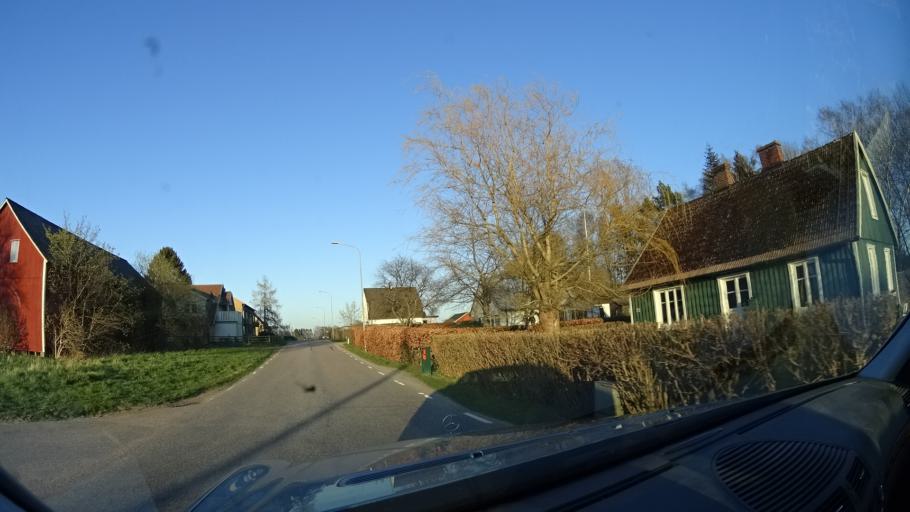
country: SE
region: Skane
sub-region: Eslovs Kommun
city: Stehag
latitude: 55.9618
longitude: 13.3261
